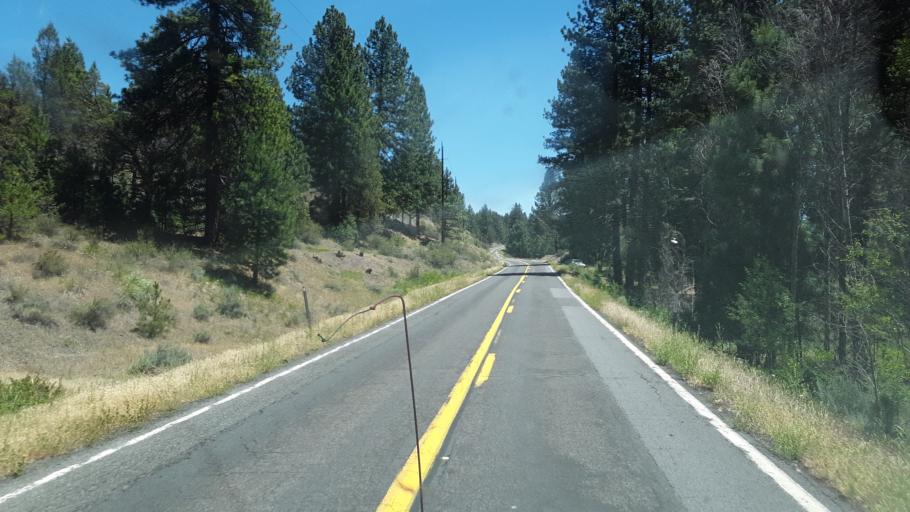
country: US
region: California
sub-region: Modoc County
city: Alturas
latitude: 41.0777
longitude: -120.8935
